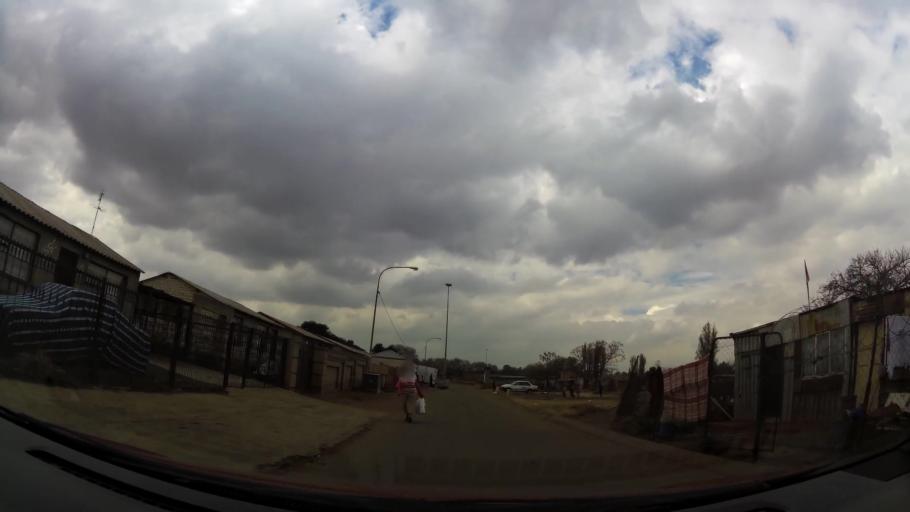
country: ZA
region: Gauteng
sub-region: City of Johannesburg Metropolitan Municipality
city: Soweto
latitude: -26.2606
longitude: 27.8410
